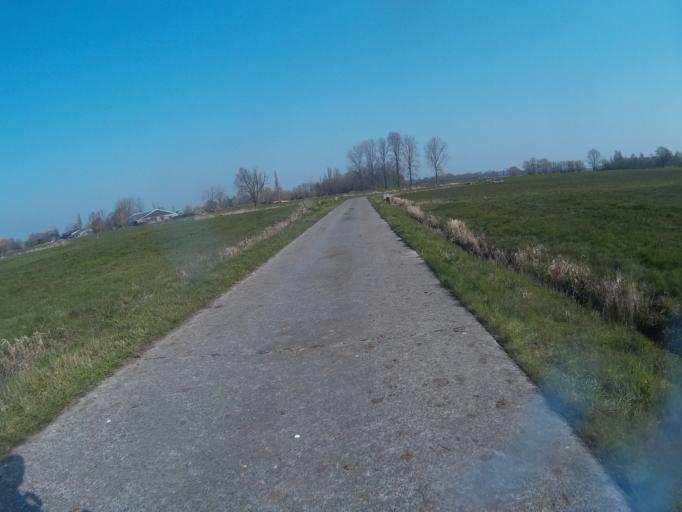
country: BE
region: Flanders
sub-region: Provincie Oost-Vlaanderen
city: Zomergem
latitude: 51.0988
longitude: 3.5139
